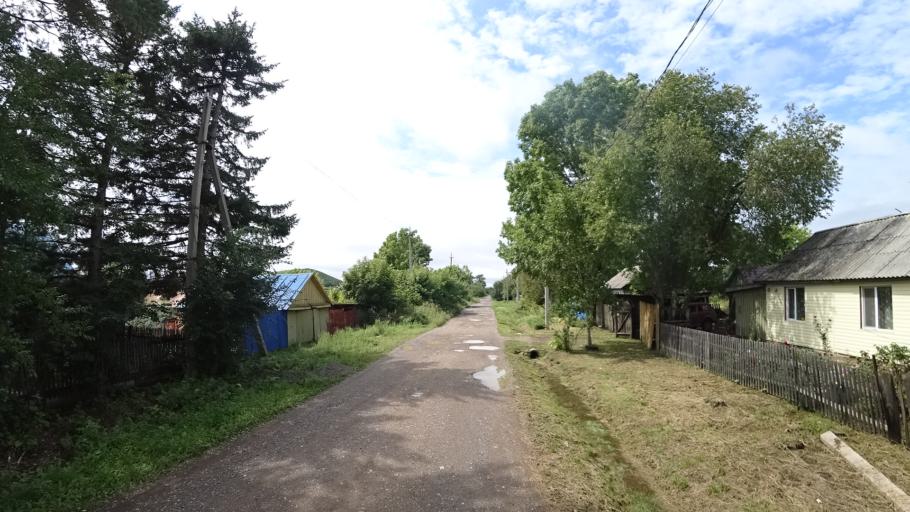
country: RU
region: Primorskiy
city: Lyalichi
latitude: 44.1389
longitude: 132.3832
